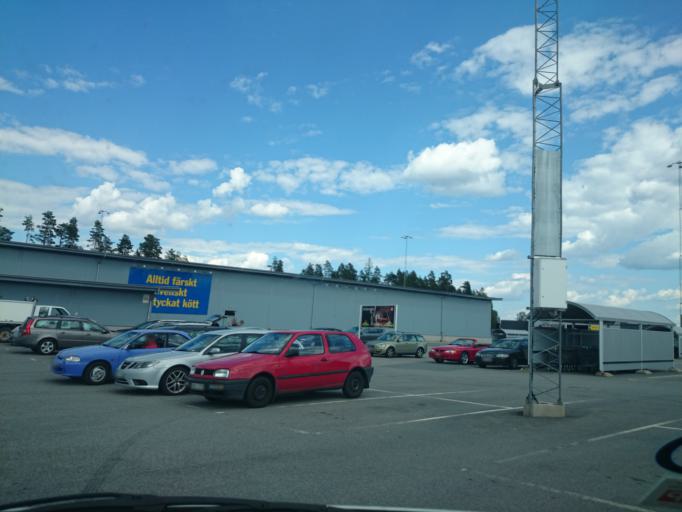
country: SE
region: Joenkoeping
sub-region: Varnamo Kommun
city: Varnamo
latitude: 57.1786
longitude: 14.0049
